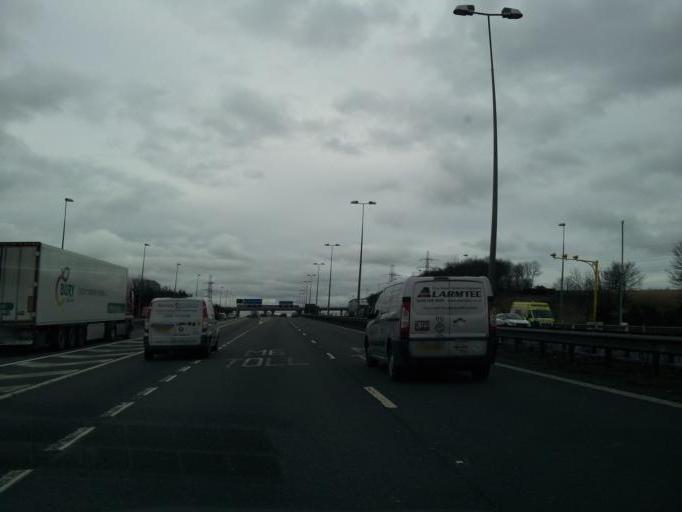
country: GB
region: England
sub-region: Staffordshire
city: Featherstone
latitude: 52.6731
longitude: -2.0803
